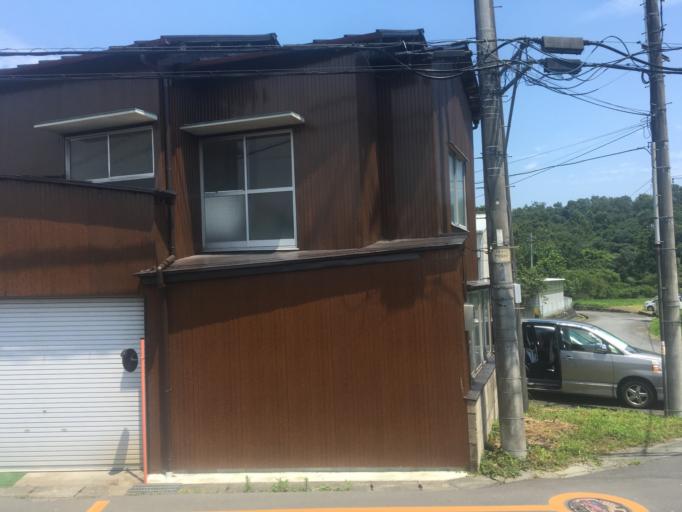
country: JP
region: Saitama
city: Yorii
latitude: 36.0952
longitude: 139.1962
